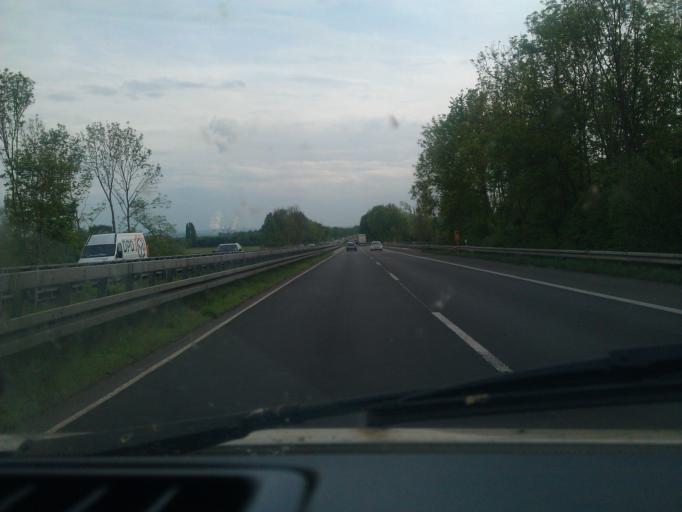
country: DE
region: North Rhine-Westphalia
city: Julich
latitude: 50.9404
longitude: 6.3435
